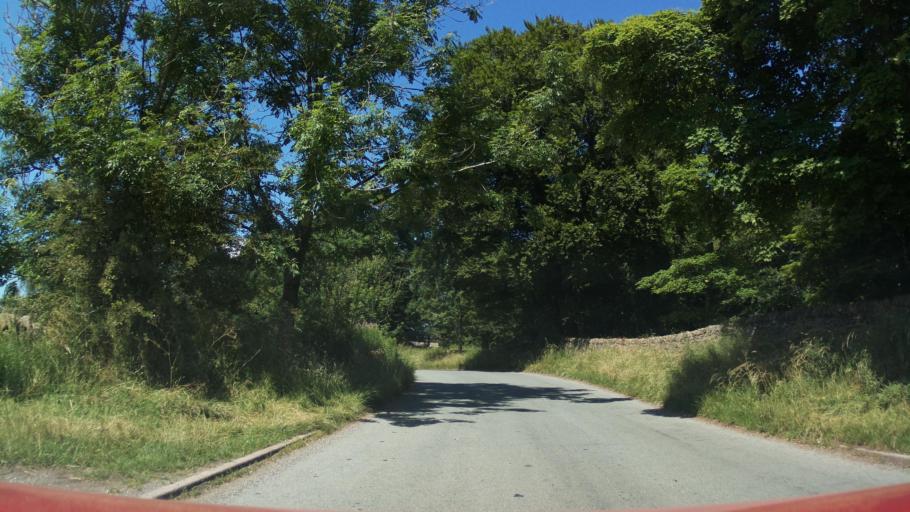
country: GB
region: England
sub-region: Derbyshire
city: Buxton
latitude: 53.1811
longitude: -1.8627
